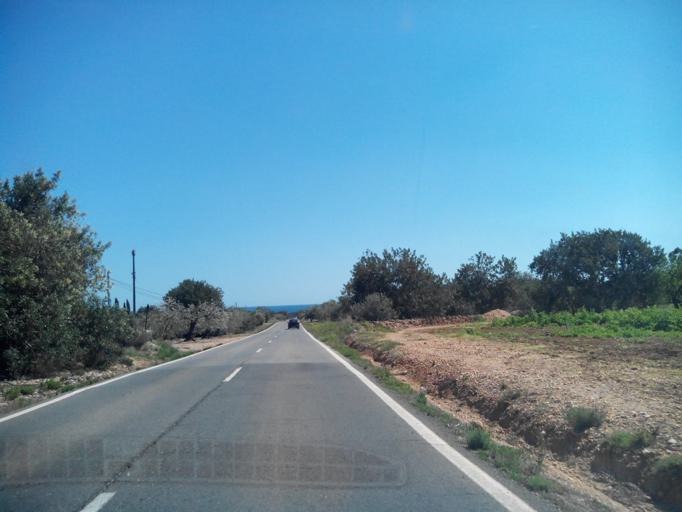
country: ES
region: Catalonia
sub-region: Provincia de Tarragona
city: Vilanova d'Escornalbou
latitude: 41.0732
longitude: 0.9748
